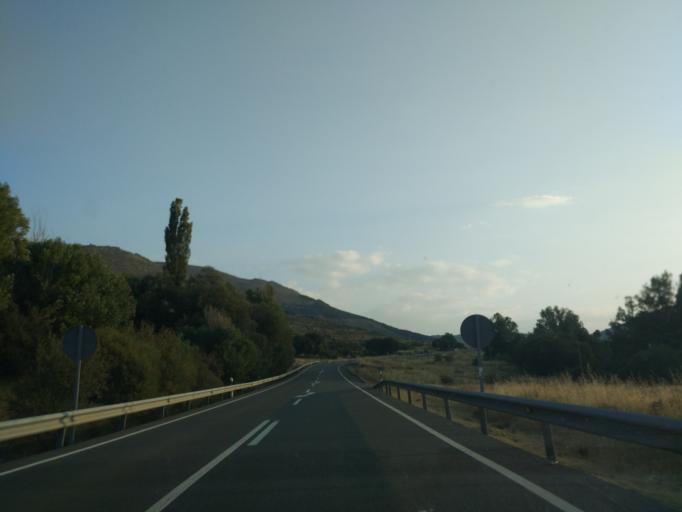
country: ES
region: Castille and Leon
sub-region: Provincia de Avila
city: Mengamunoz
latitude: 40.5123
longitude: -4.9883
